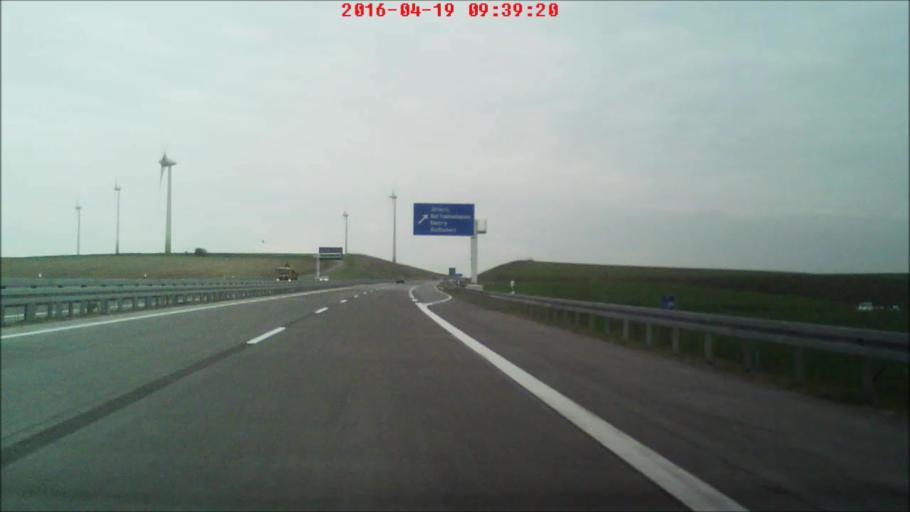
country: DE
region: Thuringia
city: Artern
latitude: 51.3760
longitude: 11.2834
